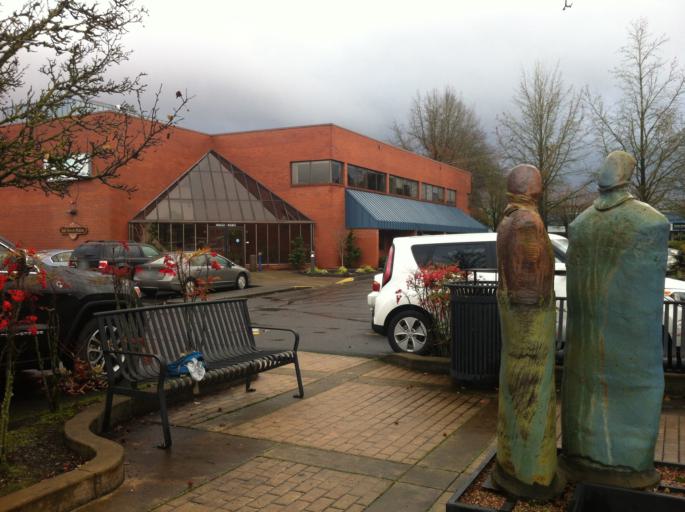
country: US
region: Oregon
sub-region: Washington County
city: Beaverton
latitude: 45.4868
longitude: -122.8039
